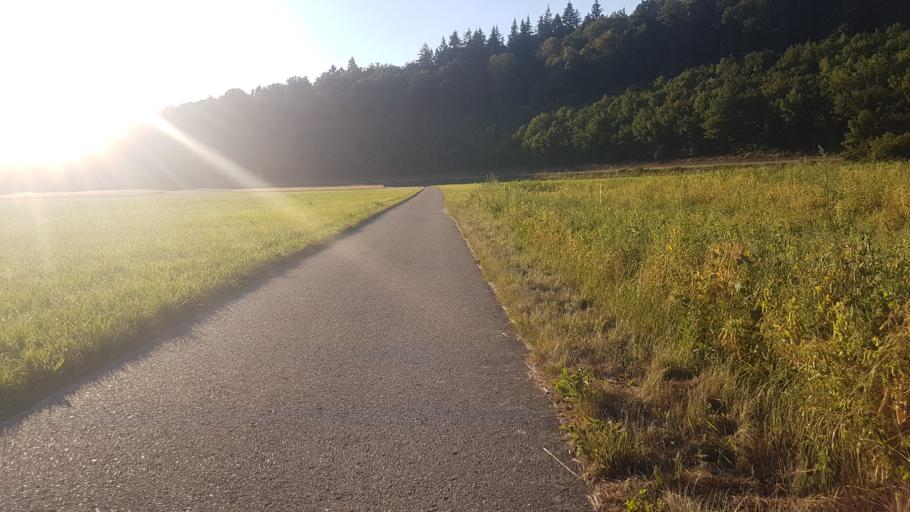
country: DE
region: Baden-Wuerttemberg
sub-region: Regierungsbezirk Stuttgart
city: Neudenau
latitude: 49.2750
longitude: 9.2375
